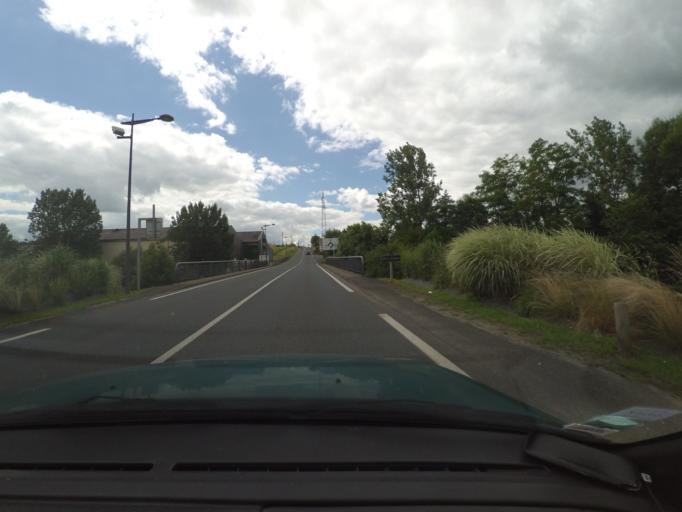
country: FR
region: Pays de la Loire
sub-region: Departement de la Loire-Atlantique
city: Mouzillon
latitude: 47.1385
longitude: -1.2824
